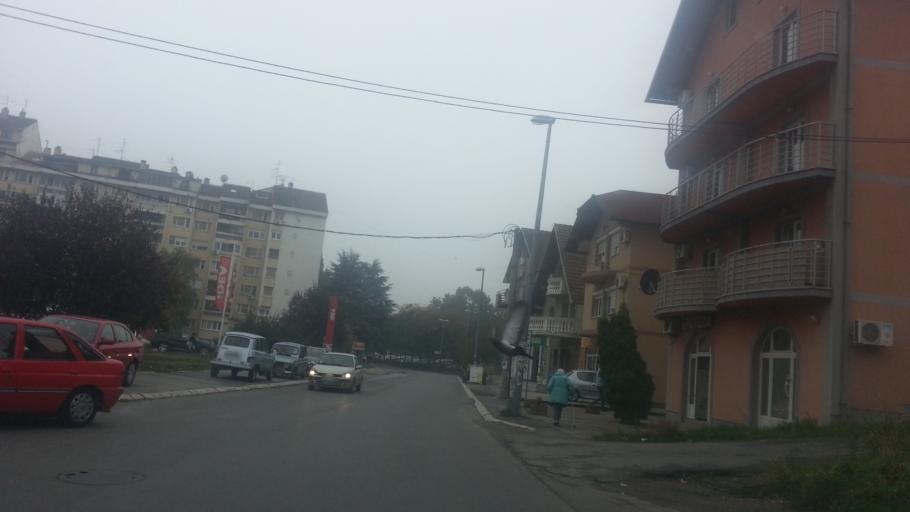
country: RS
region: Central Serbia
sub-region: Belgrade
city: Zemun
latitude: 44.8469
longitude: 20.3804
